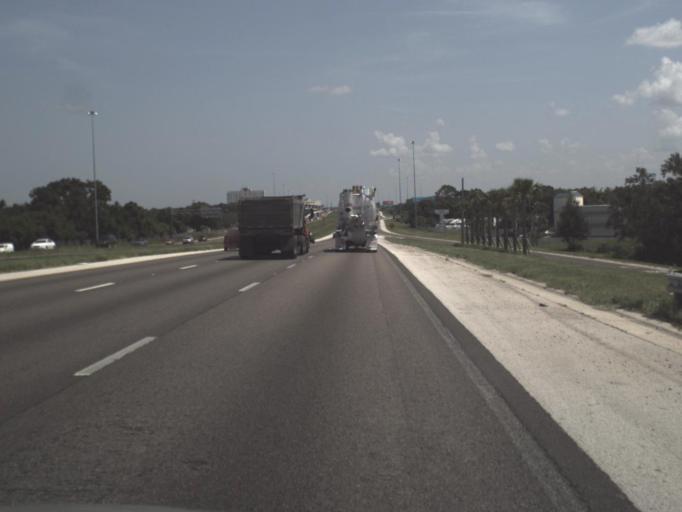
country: US
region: Florida
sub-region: Hillsborough County
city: East Lake-Orient Park
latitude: 27.9822
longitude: -82.3830
